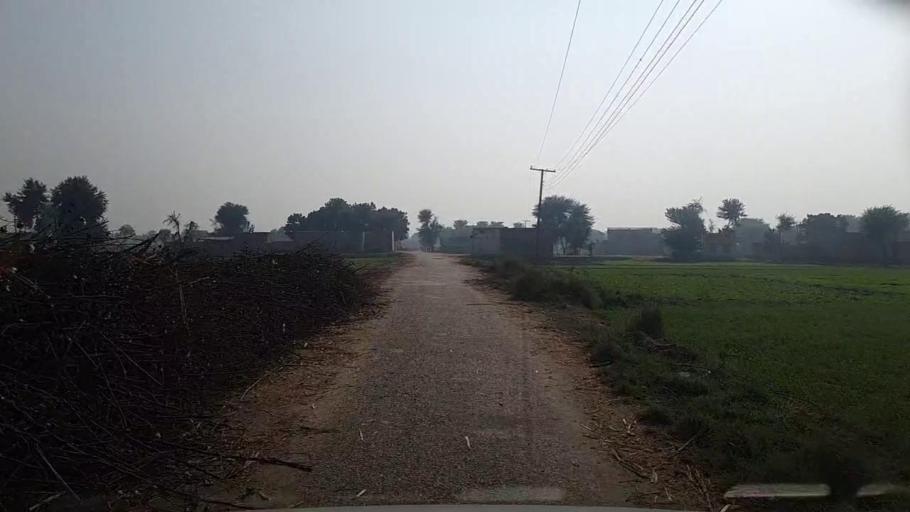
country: PK
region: Sindh
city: Setharja Old
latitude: 27.1216
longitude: 68.5160
